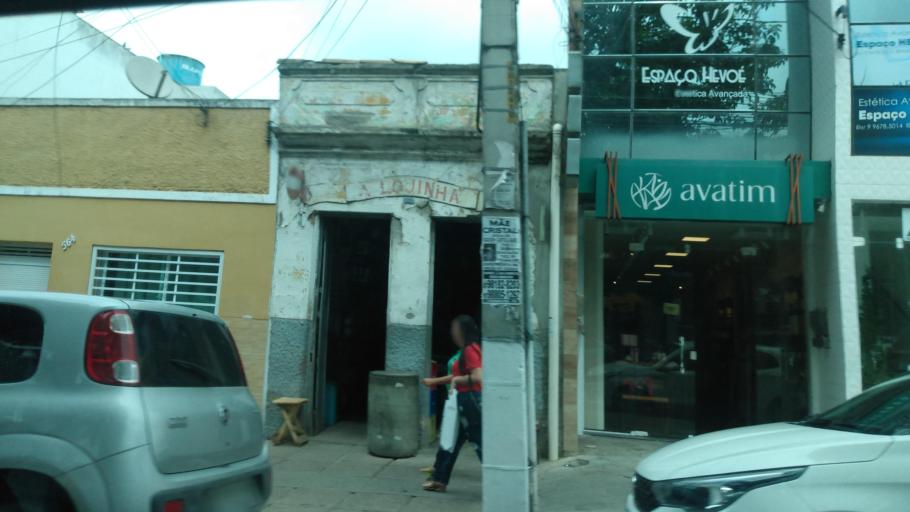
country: BR
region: Pernambuco
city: Garanhuns
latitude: -8.8849
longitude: -36.4828
